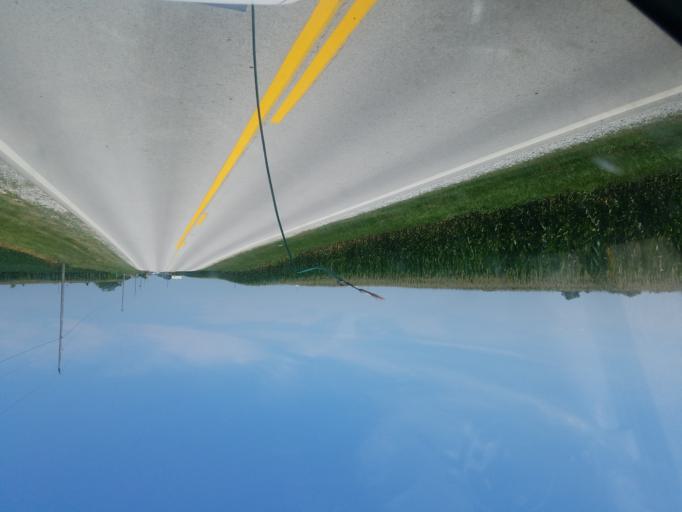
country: US
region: Ohio
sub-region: Auglaize County
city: New Bremen
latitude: 40.4322
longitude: -84.4338
